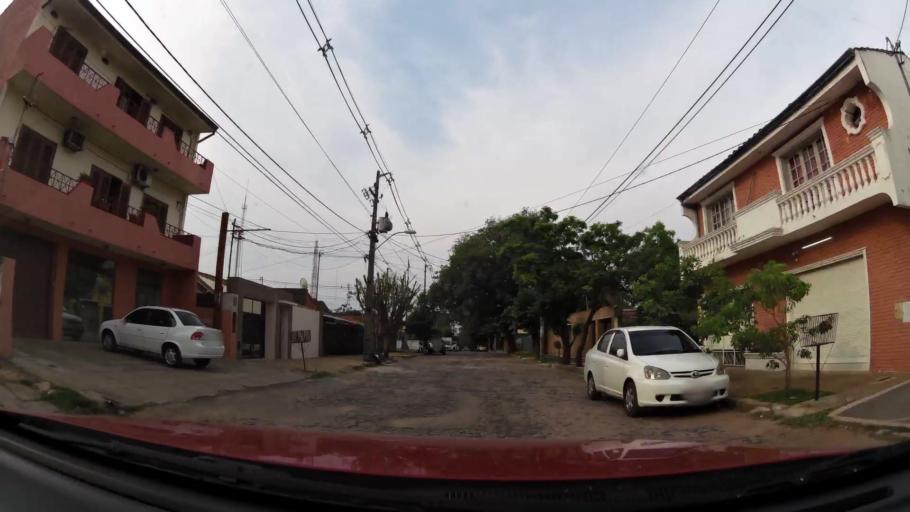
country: PY
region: Asuncion
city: Asuncion
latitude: -25.3030
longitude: -57.6089
